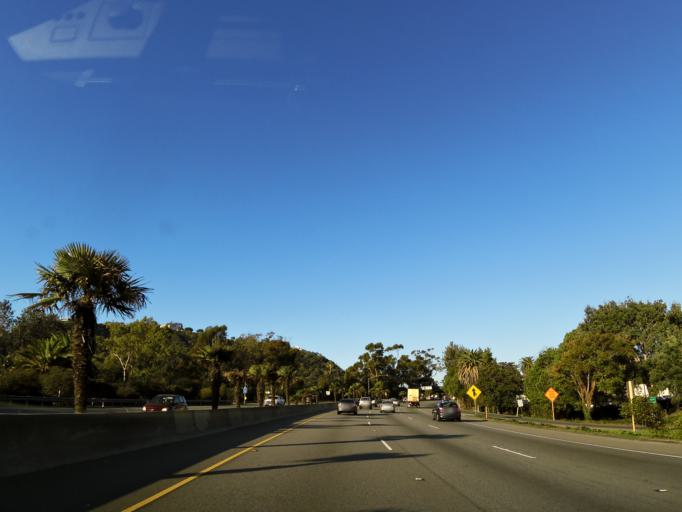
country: US
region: California
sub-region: Santa Barbara County
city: Santa Barbara
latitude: 34.4122
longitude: -119.6996
